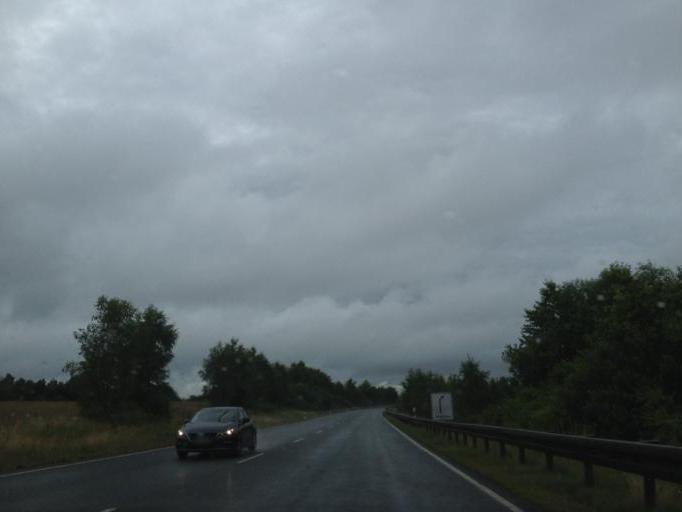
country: DE
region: Bavaria
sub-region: Upper Franconia
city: Hohenberg an der Eger
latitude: 50.0808
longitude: 12.2022
